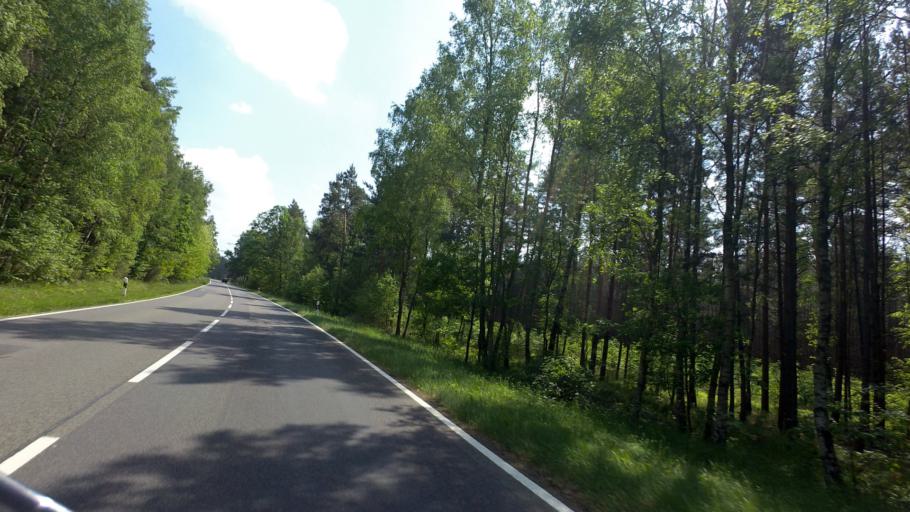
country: DE
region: Saxony
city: Schleife
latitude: 51.5642
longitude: 14.4859
